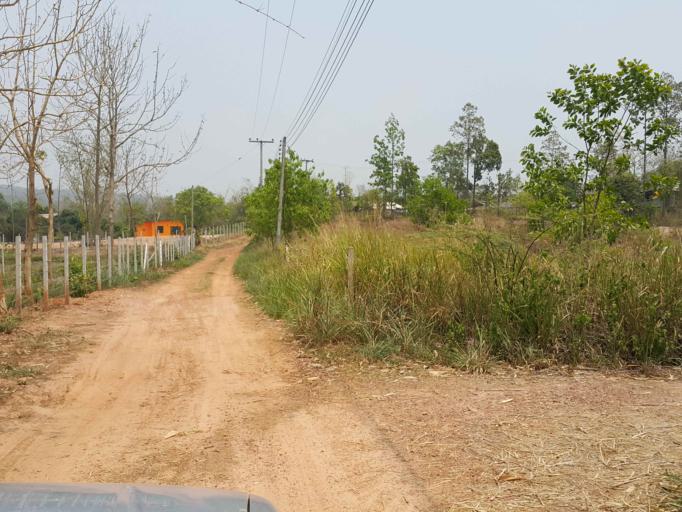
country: TH
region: Chiang Mai
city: San Sai
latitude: 18.9325
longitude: 99.0325
